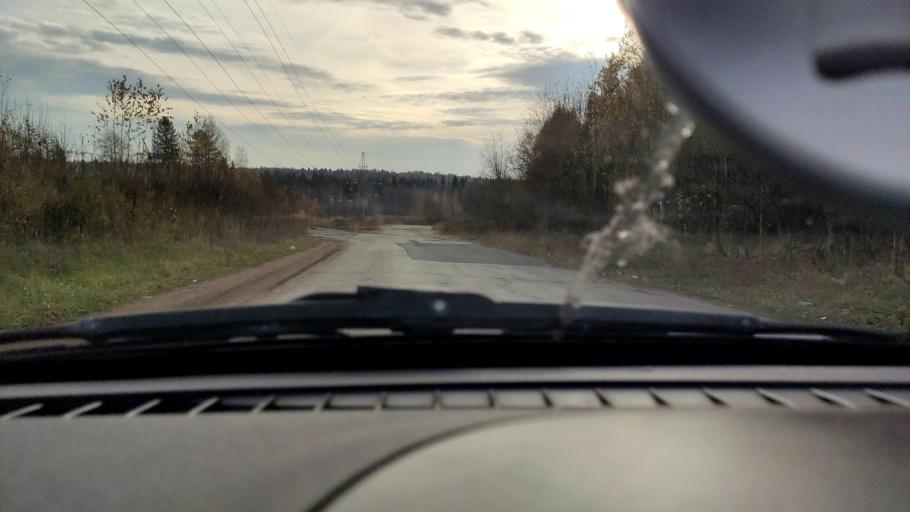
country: RU
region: Perm
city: Perm
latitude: 58.0890
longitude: 56.4176
